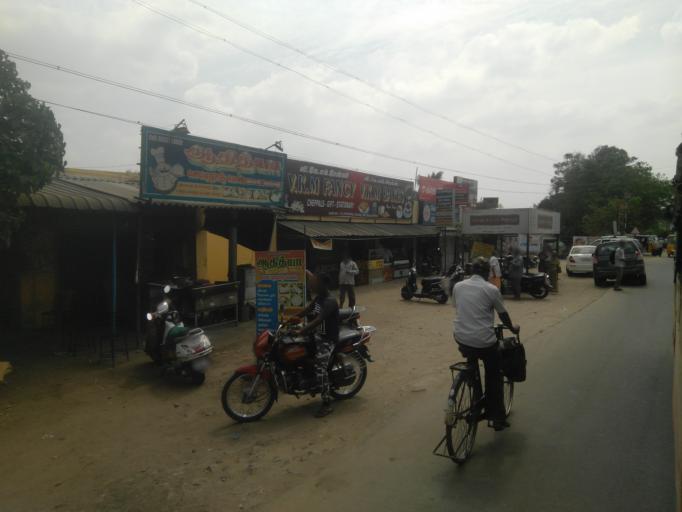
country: IN
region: Tamil Nadu
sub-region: Coimbatore
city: Irugur
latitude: 11.0046
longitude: 77.0661
